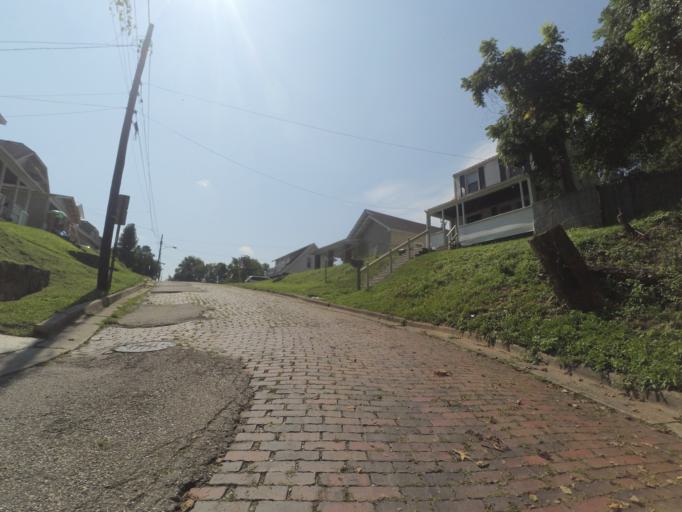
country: US
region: West Virginia
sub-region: Cabell County
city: Huntington
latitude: 38.4126
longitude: -82.4109
